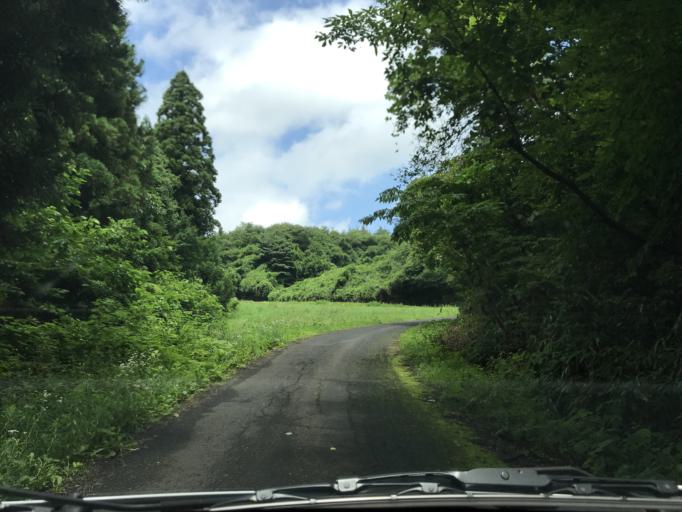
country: JP
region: Iwate
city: Mizusawa
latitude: 39.0569
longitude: 141.3809
